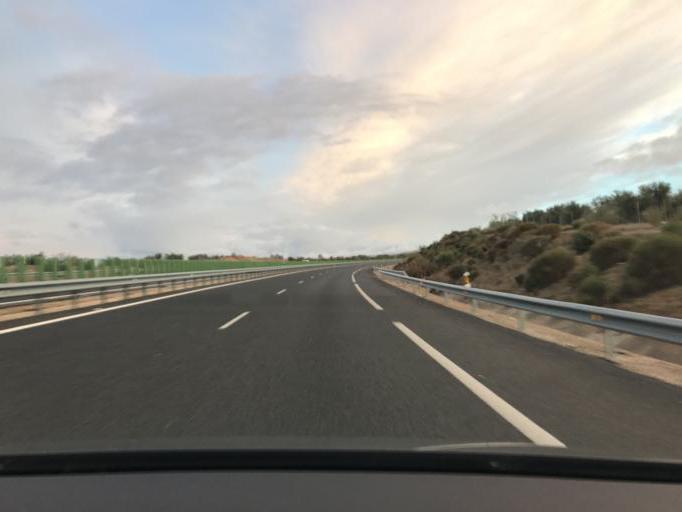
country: ES
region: Andalusia
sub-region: Provincia de Jaen
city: Jaen
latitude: 37.8169
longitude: -3.7382
